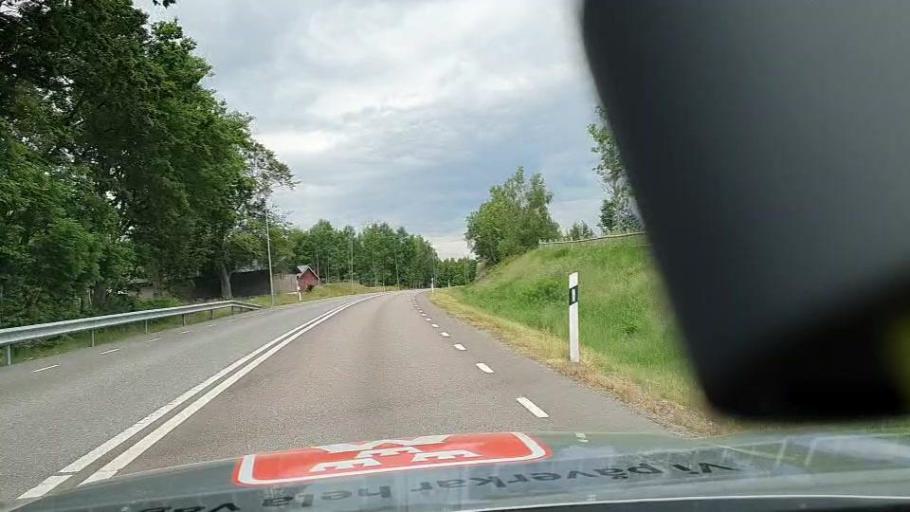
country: SE
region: Blekinge
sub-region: Karlskrona Kommun
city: Rodeby
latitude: 56.4326
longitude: 15.5386
